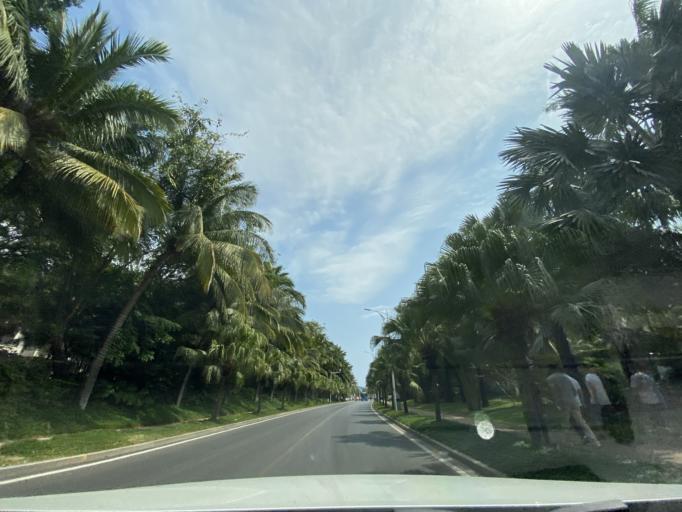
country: CN
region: Hainan
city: Tiandu
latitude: 18.2331
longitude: 109.6374
